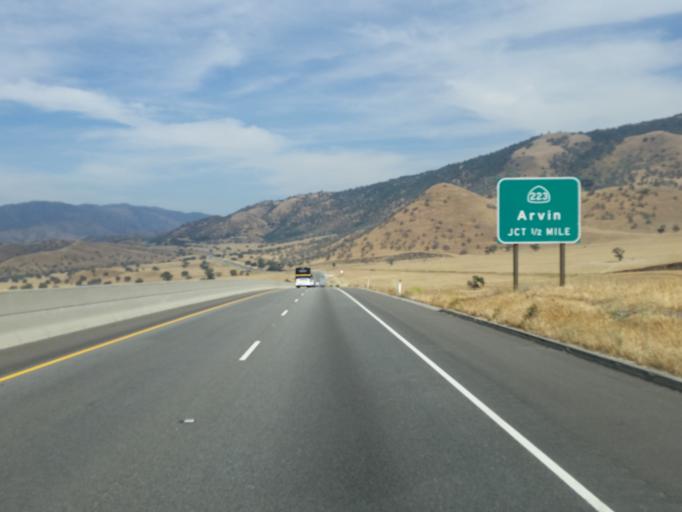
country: US
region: California
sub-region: Kern County
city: Bear Valley Springs
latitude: 35.2681
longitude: -118.6730
